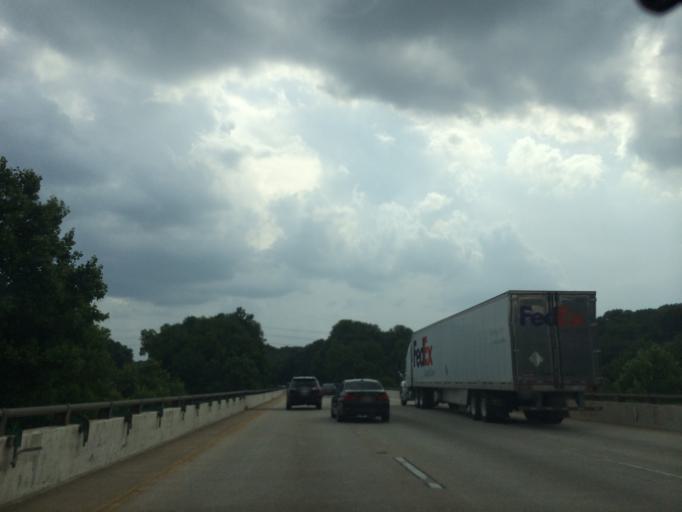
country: US
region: Maryland
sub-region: Howard County
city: Ellicott City
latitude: 39.3055
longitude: -76.7949
